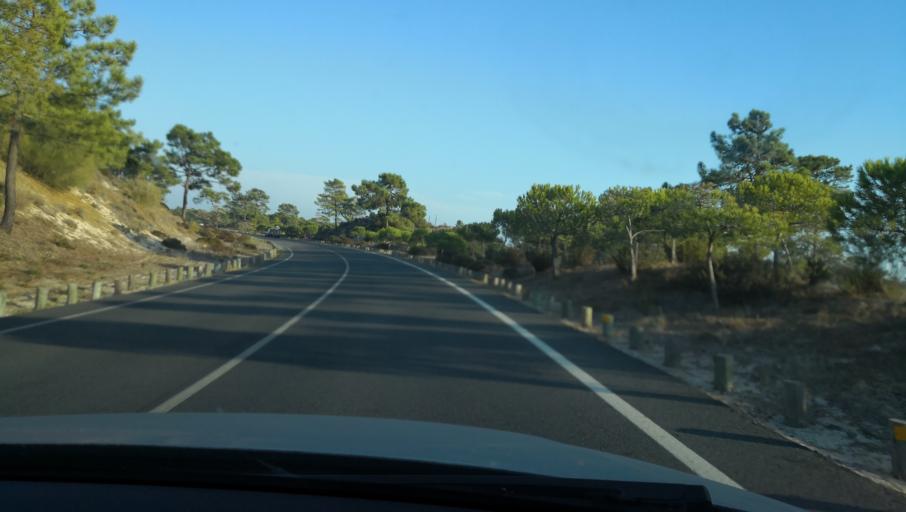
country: PT
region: Setubal
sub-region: Setubal
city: Setubal
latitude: 38.4695
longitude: -8.8833
